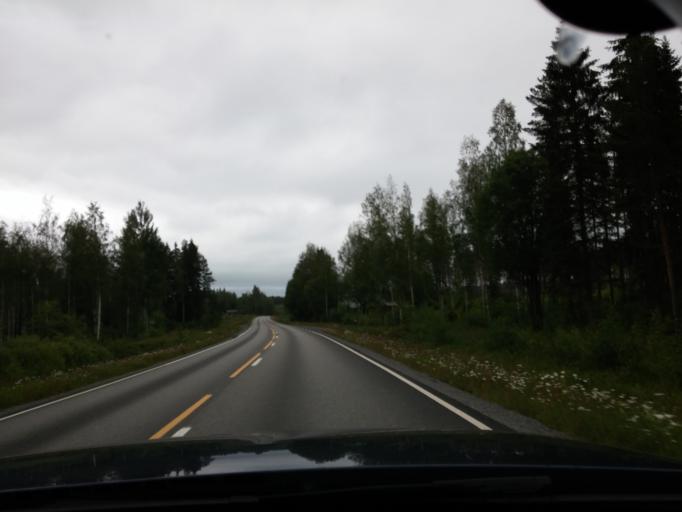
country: FI
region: Central Finland
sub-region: Saarijaervi-Viitasaari
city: Saarijaervi
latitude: 62.6798
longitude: 25.2303
